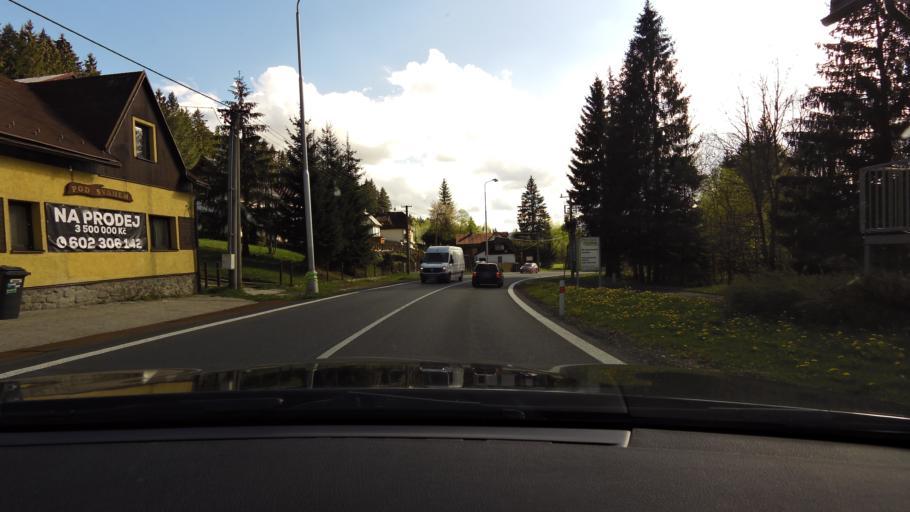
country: CZ
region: Plzensky
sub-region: Okres Klatovy
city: Zelezna Ruda
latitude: 49.1406
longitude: 13.2441
